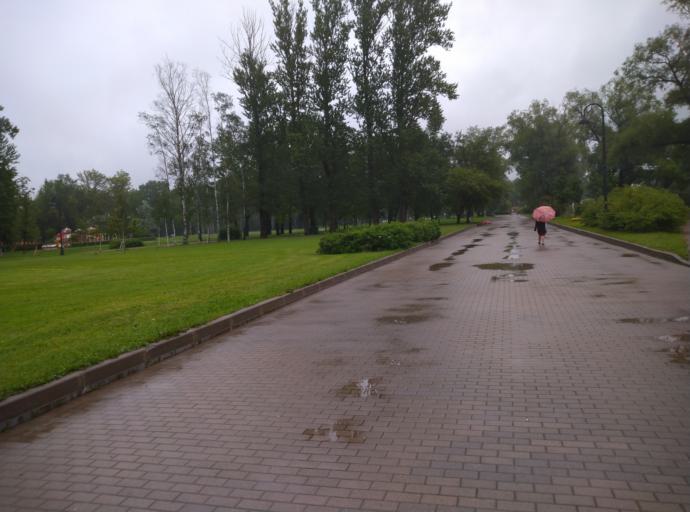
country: RU
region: St.-Petersburg
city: Kupchino
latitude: 59.8676
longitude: 30.3297
